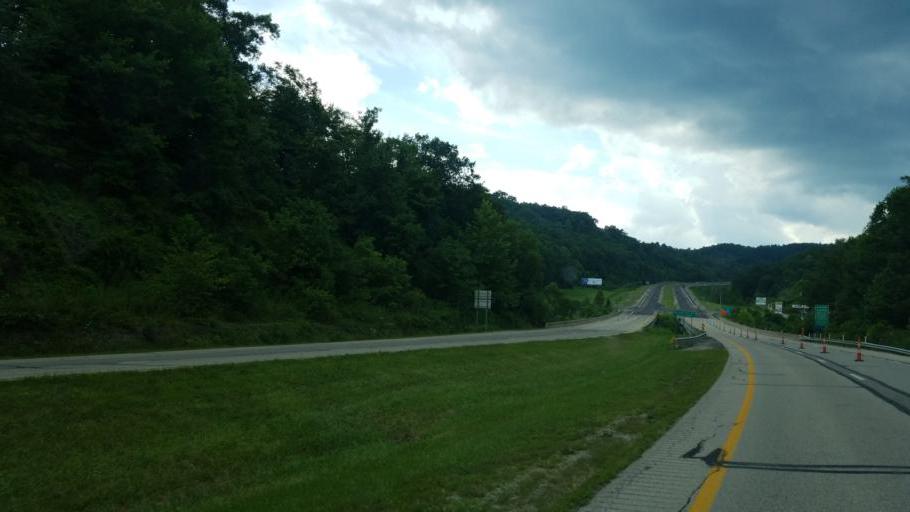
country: US
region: West Virginia
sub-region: Kanawha County
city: Alum Creek
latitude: 38.2680
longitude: -81.8031
